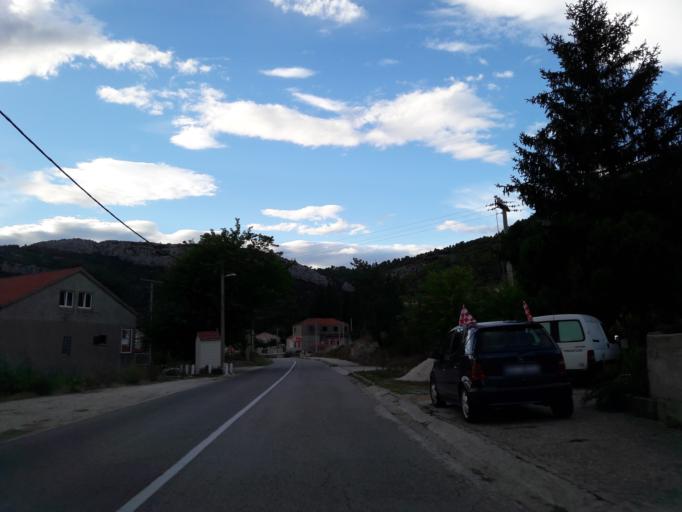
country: HR
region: Dubrovacko-Neretvanska
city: Ston
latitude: 42.8436
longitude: 17.6312
